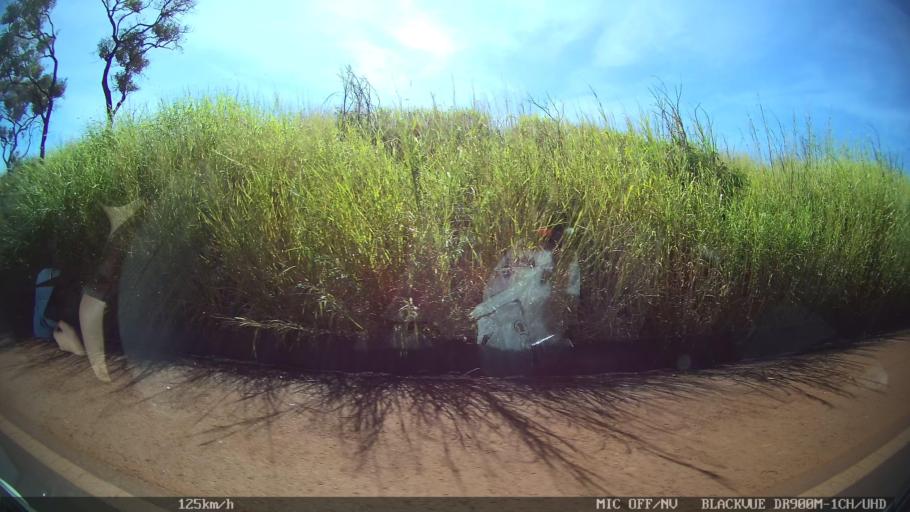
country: BR
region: Sao Paulo
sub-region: Sao Joaquim Da Barra
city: Sao Joaquim da Barra
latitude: -20.5429
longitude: -47.7943
